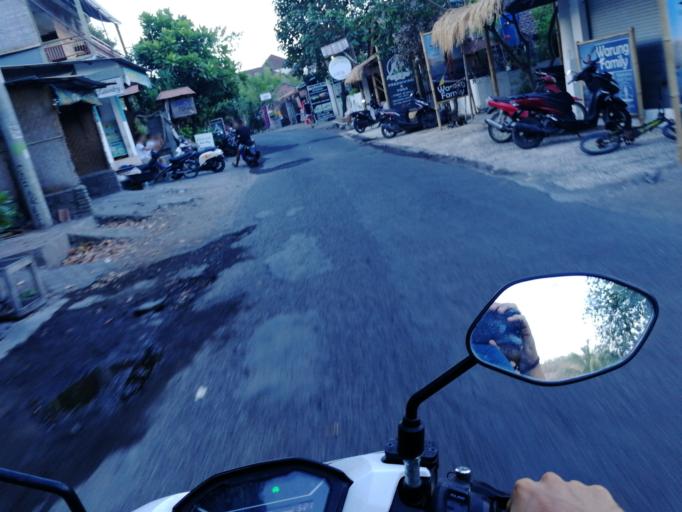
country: ID
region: Bali
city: Biaslantang Kaler
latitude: -8.3372
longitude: 115.6587
